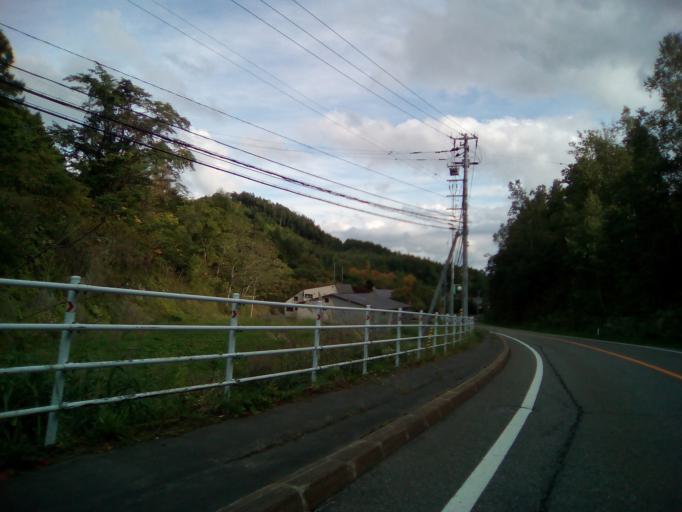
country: JP
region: Hokkaido
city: Date
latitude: 42.6561
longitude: 140.8285
